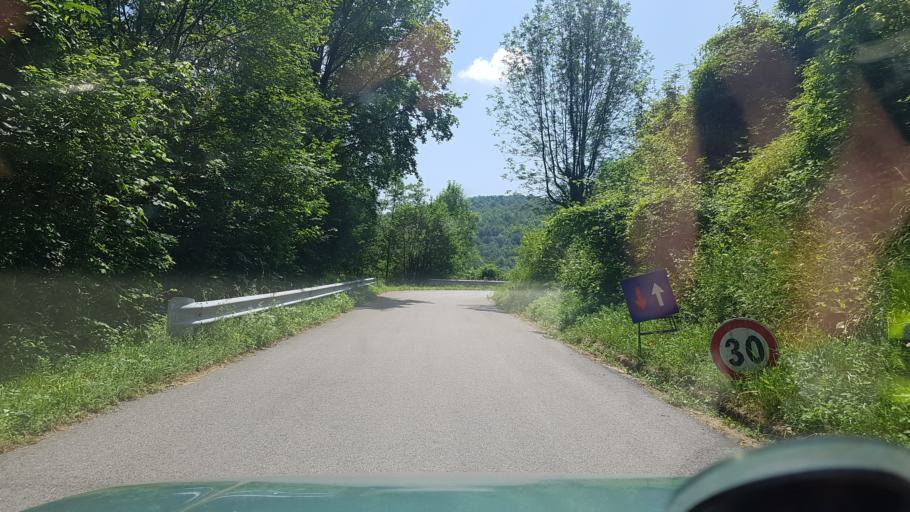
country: IT
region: Friuli Venezia Giulia
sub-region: Provincia di Udine
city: Lusevera
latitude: 46.2741
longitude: 13.2930
